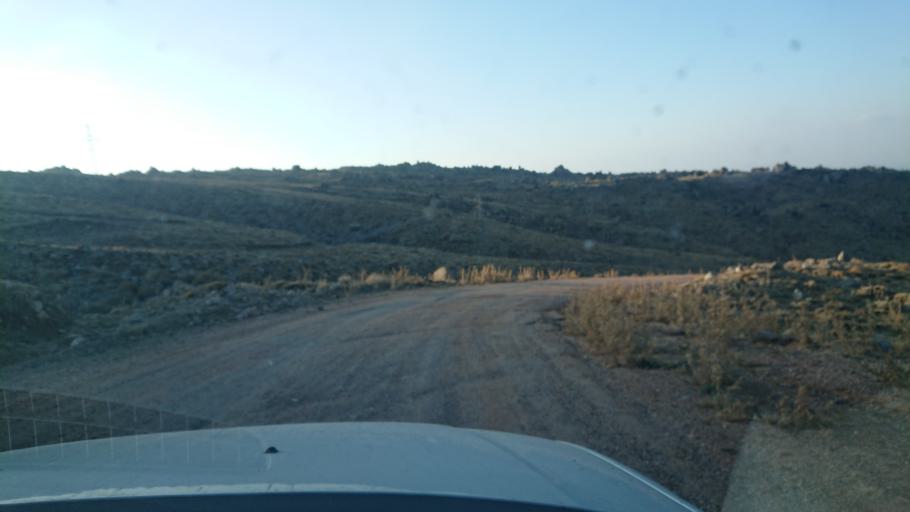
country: TR
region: Aksaray
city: Taspinar
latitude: 38.1600
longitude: 34.1716
